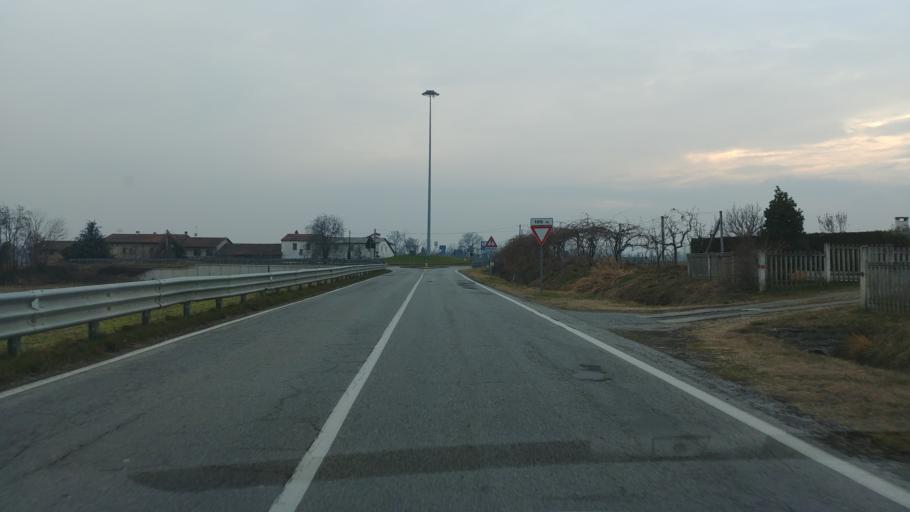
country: IT
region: Piedmont
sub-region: Provincia di Cuneo
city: Castelletto Stura
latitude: 44.4591
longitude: 7.6284
